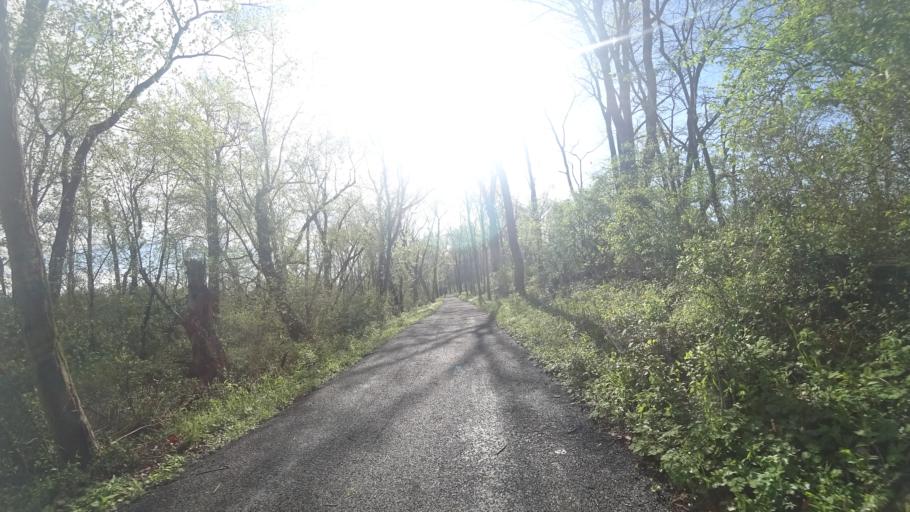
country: US
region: Virginia
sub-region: Loudoun County
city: University Center
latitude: 39.0761
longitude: -77.4298
